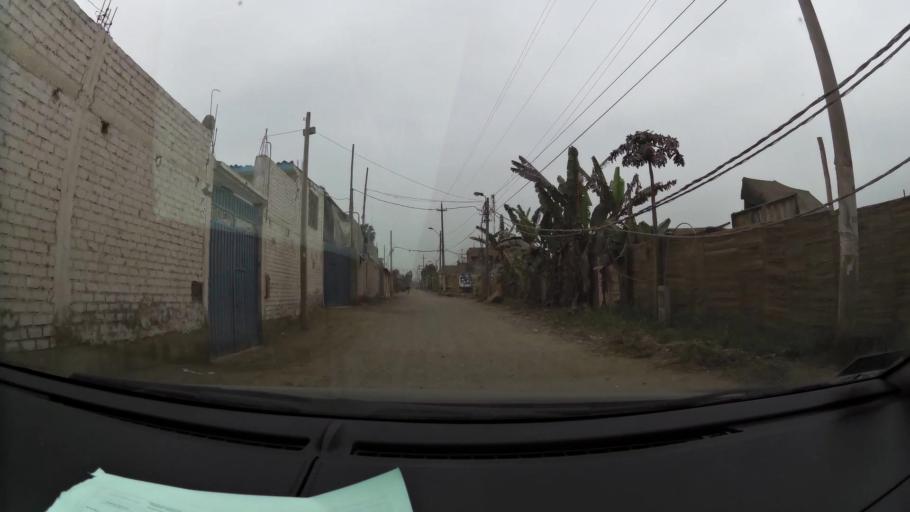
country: PE
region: Lima
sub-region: Lima
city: Urb. Santo Domingo
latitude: -11.8949
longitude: -77.0627
